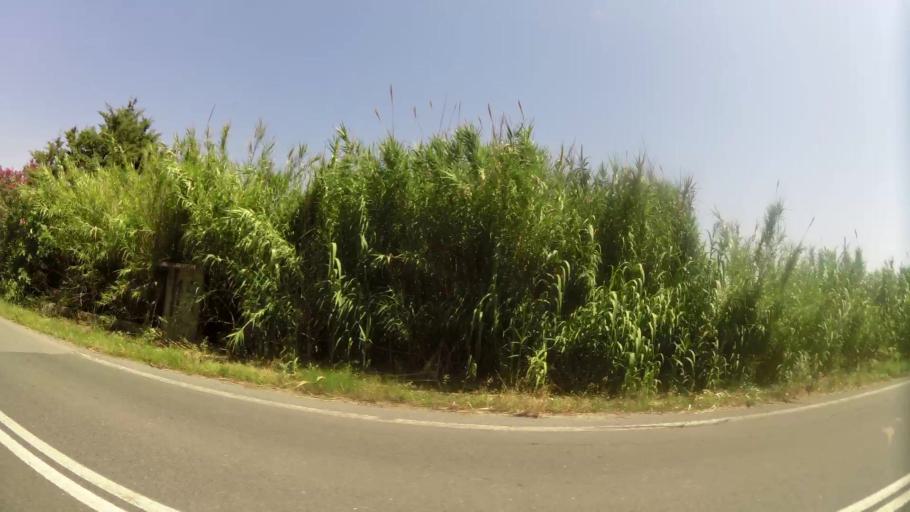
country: GR
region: Central Macedonia
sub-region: Nomos Thessalonikis
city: Trilofos
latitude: 40.4758
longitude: 22.9733
